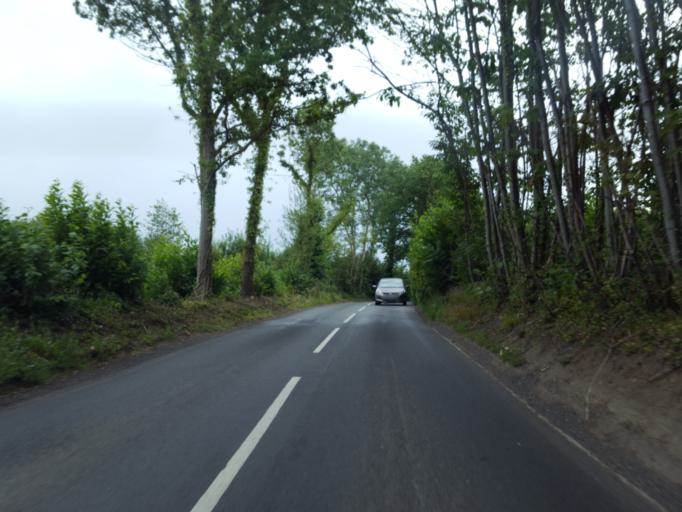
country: GB
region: England
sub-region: Kent
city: Maidstone
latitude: 51.2335
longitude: 0.4796
